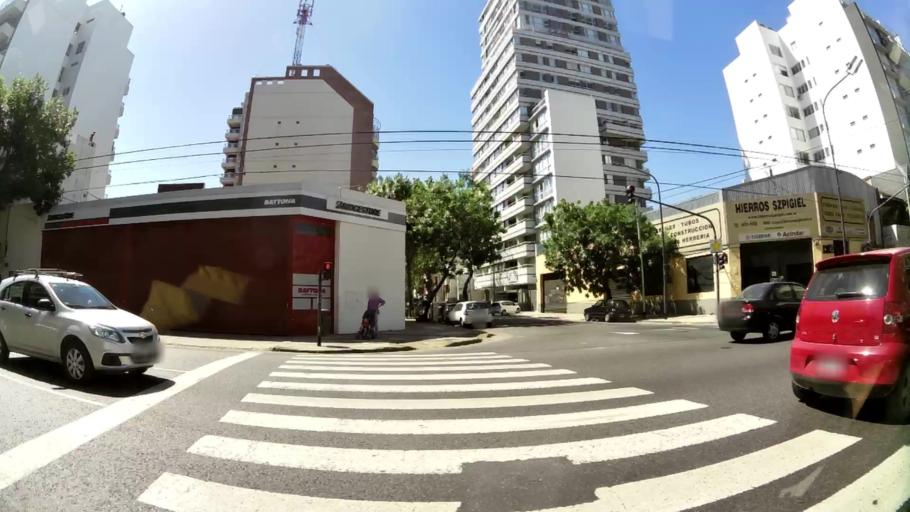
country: AR
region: Buenos Aires F.D.
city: Villa Santa Rita
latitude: -34.6303
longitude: -58.4494
